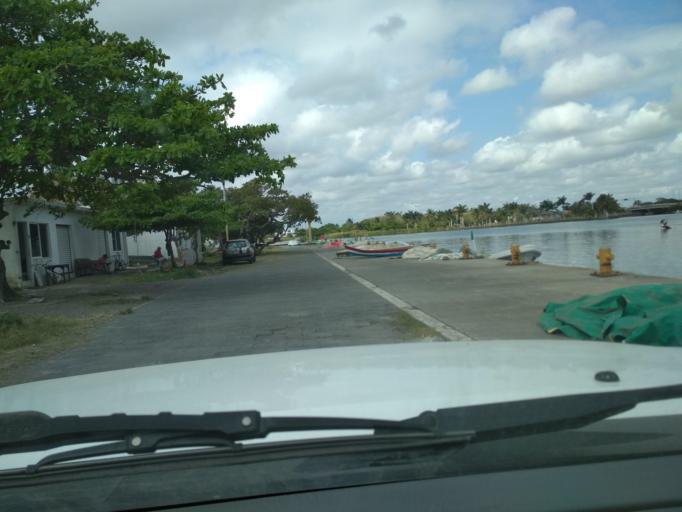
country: MX
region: Veracruz
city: Boca del Rio
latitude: 19.0980
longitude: -96.1077
